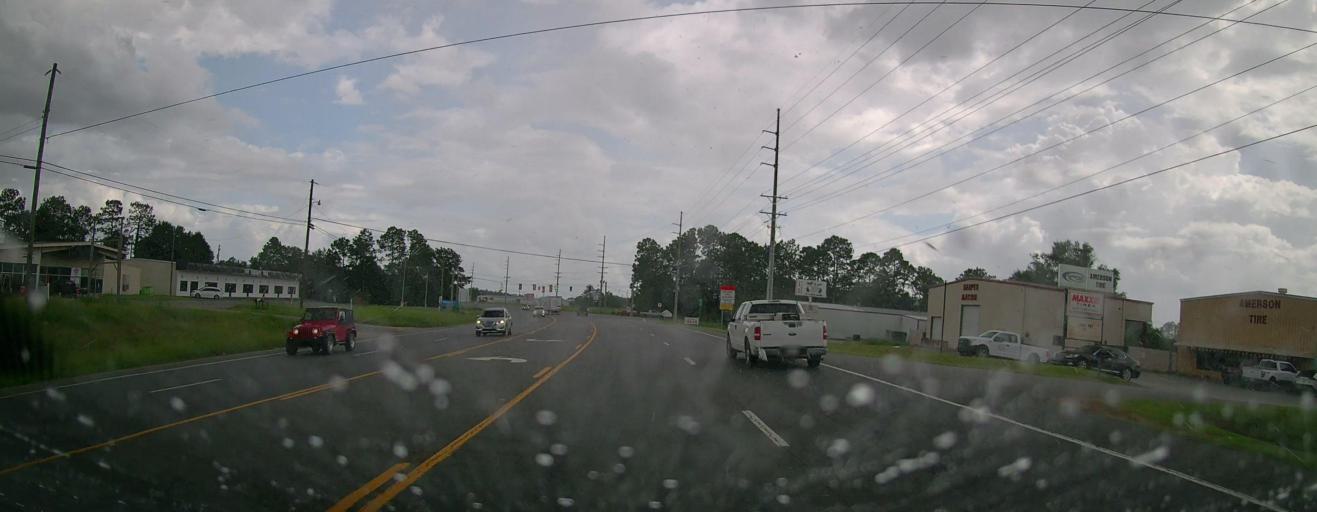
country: US
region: Georgia
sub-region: Coffee County
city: Douglas
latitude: 31.5041
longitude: -82.8750
